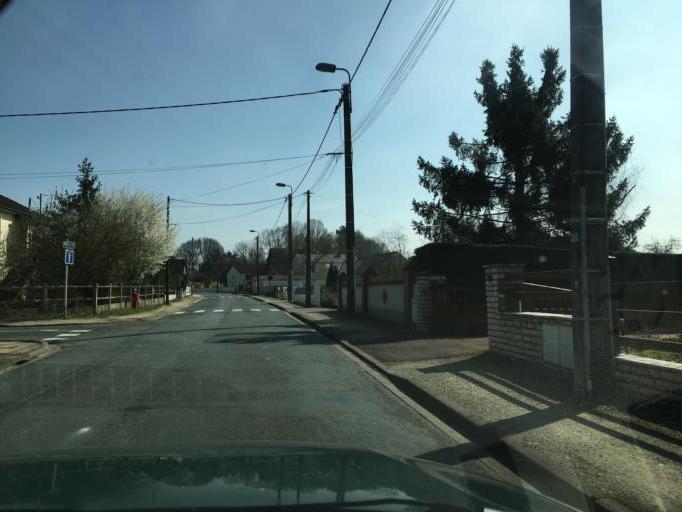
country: FR
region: Centre
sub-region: Departement du Loiret
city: Saran
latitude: 47.9536
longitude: 1.8986
